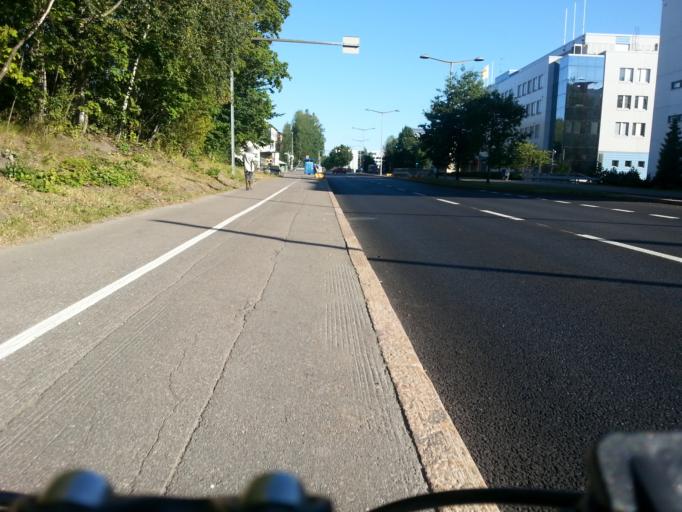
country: FI
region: Uusimaa
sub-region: Helsinki
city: Teekkarikylae
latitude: 60.2182
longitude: 24.8675
